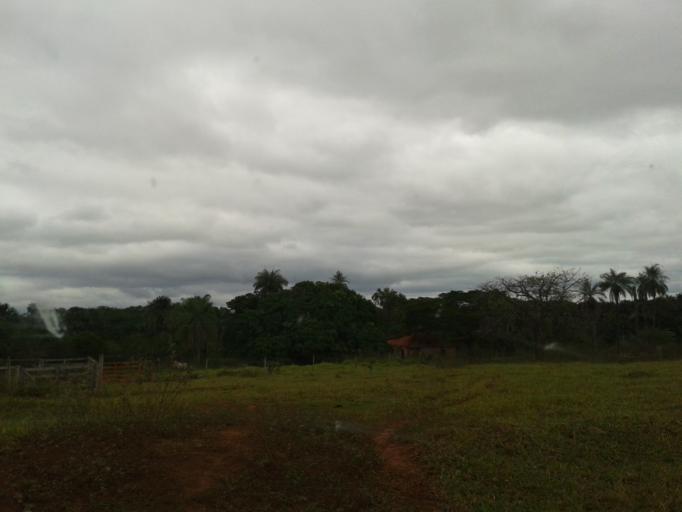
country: BR
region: Minas Gerais
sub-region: Campina Verde
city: Campina Verde
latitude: -19.5043
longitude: -49.6420
